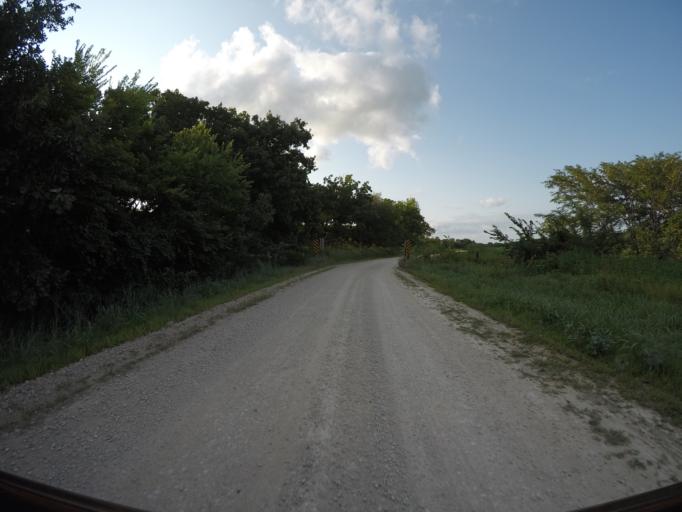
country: US
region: Kansas
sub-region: Wabaunsee County
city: Alma
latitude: 38.8843
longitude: -96.2083
